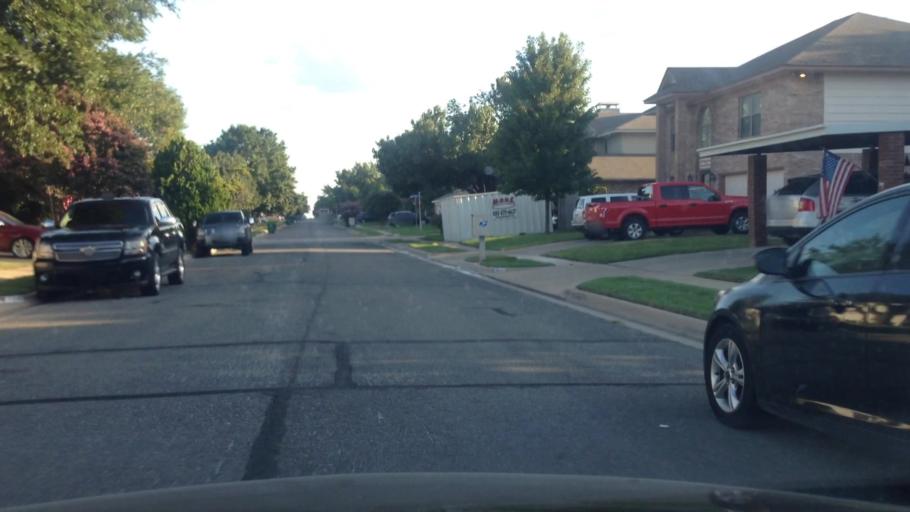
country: US
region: Texas
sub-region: Tarrant County
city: Watauga
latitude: 32.8731
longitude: -97.2490
